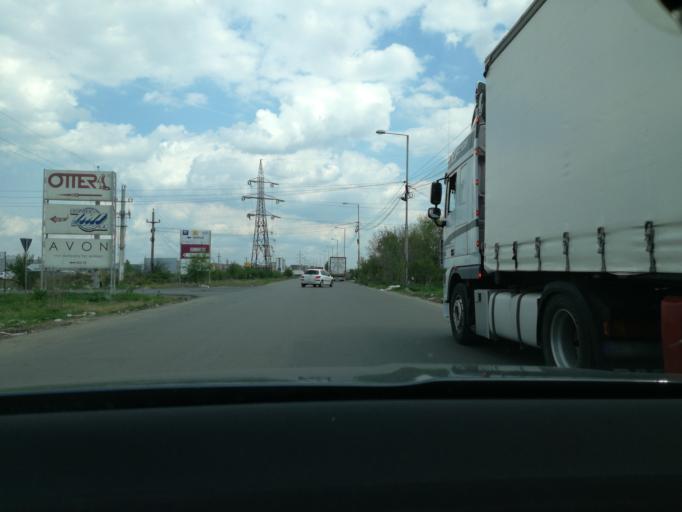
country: RO
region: Ilfov
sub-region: Comuna Chiajna
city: Chiajna
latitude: 44.4407
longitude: 25.9613
